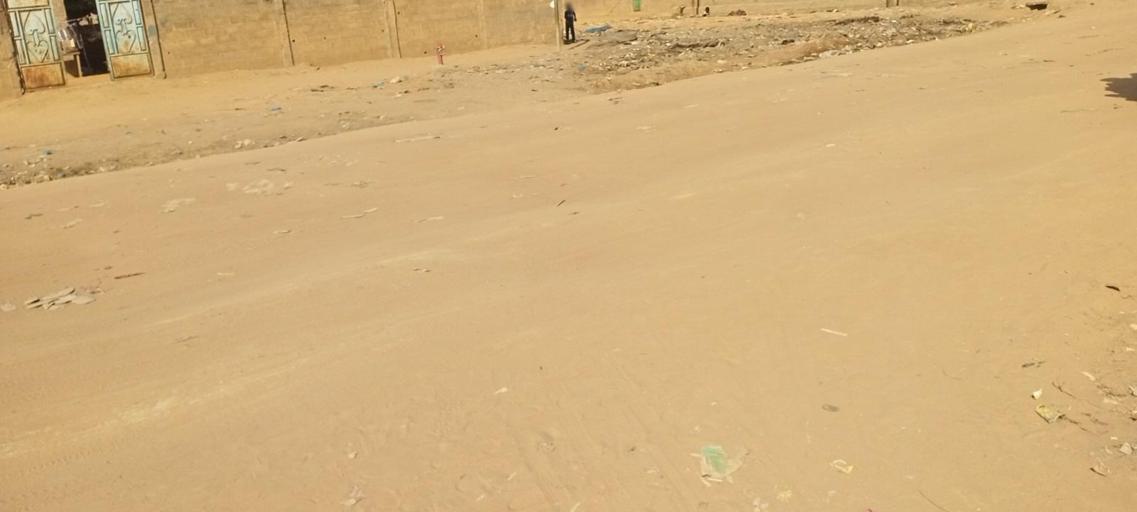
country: TD
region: Chari-Baguirmi
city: N'Djamena
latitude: 12.1130
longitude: 15.1141
